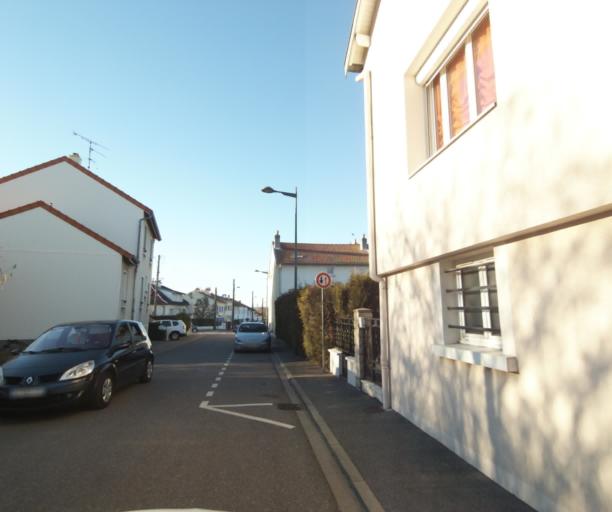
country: FR
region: Lorraine
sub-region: Departement de Meurthe-et-Moselle
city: Laneuveville-devant-Nancy
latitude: 48.6528
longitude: 6.2264
